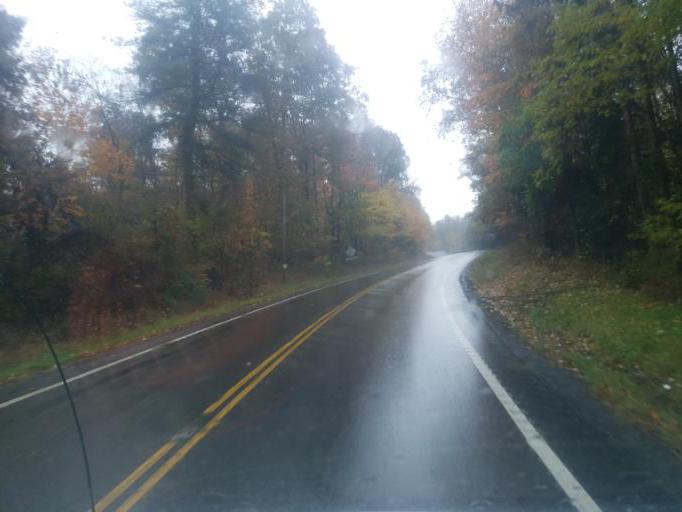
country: US
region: Ohio
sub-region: Licking County
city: Utica
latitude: 40.2281
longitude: -82.2670
